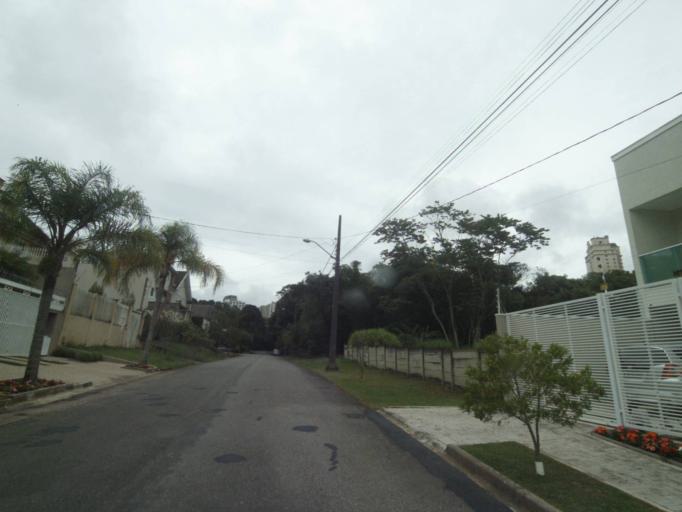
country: BR
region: Parana
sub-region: Curitiba
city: Curitiba
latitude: -25.4421
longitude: -49.3313
